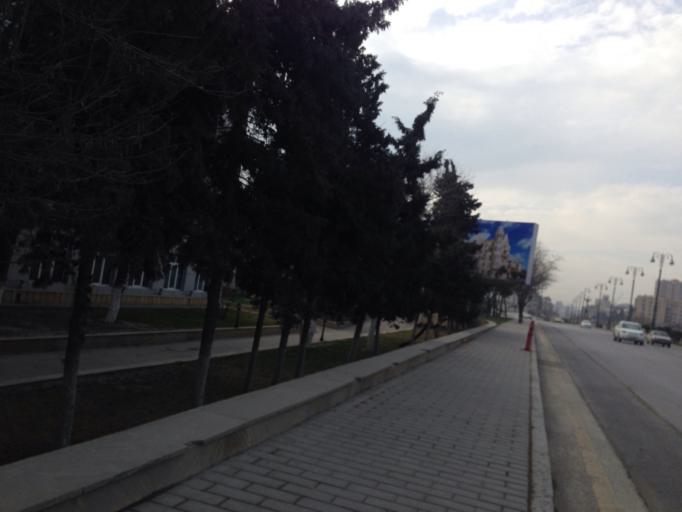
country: AZ
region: Baki
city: Baku
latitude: 40.4047
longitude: 49.8858
